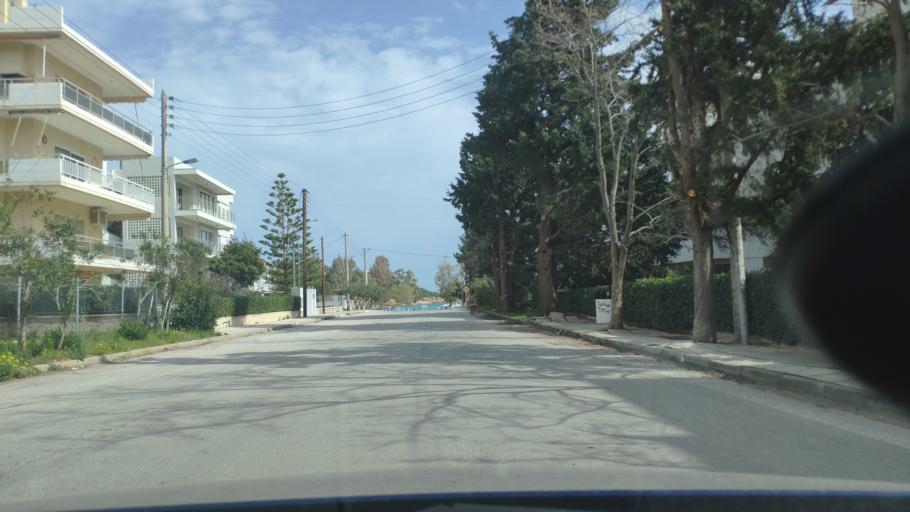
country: GR
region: Attica
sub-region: Nomarchia Anatolikis Attikis
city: Limin Mesoyaias
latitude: 37.8923
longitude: 24.0224
